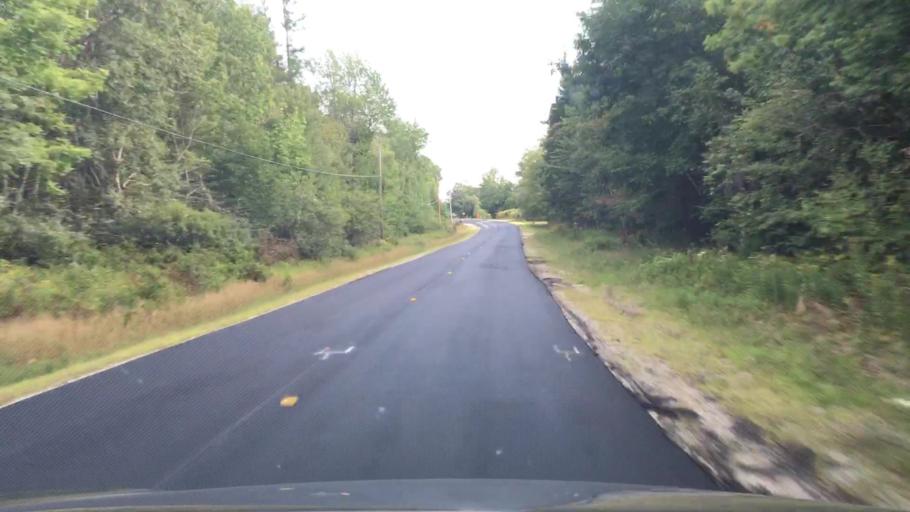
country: US
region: Maine
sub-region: Hancock County
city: Orland
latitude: 44.5497
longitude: -68.6209
